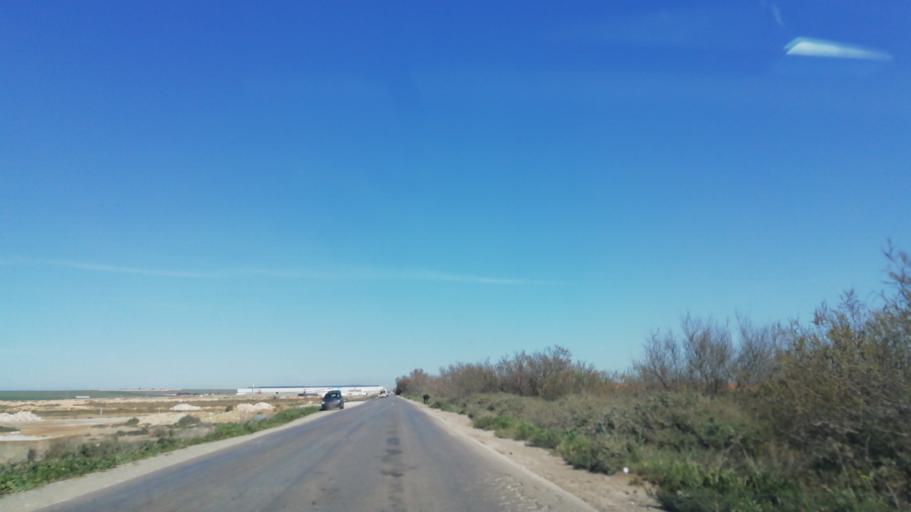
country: DZ
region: Oran
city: Es Senia
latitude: 35.5005
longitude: -0.5953
